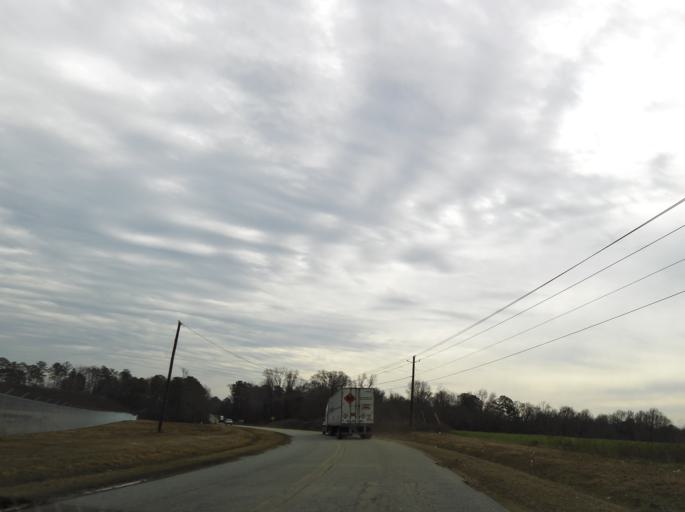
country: US
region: Georgia
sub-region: Houston County
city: Centerville
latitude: 32.6838
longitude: -83.6629
